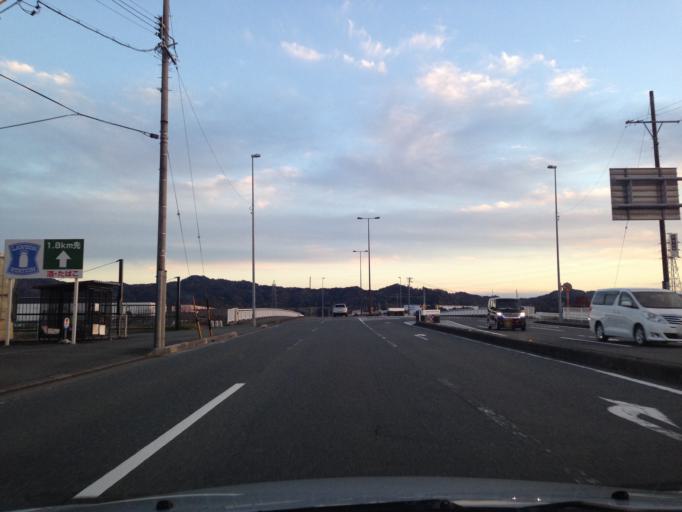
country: JP
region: Shizuoka
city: Kakegawa
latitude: 34.7627
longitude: 137.9706
